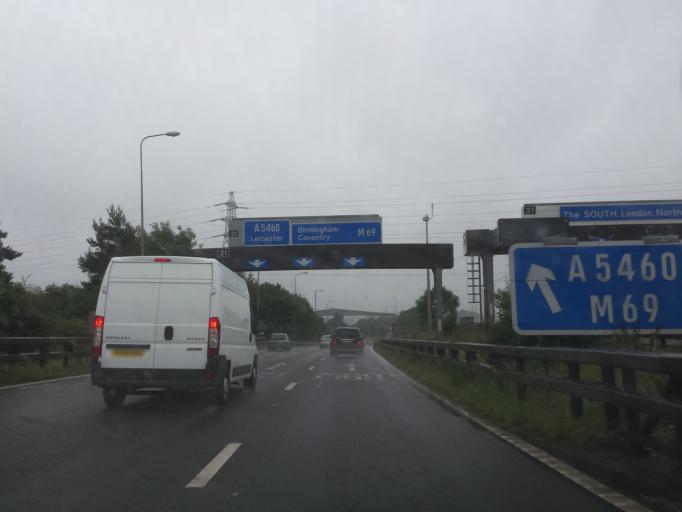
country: GB
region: England
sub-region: Leicestershire
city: Enderby
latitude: 52.6035
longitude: -1.1953
